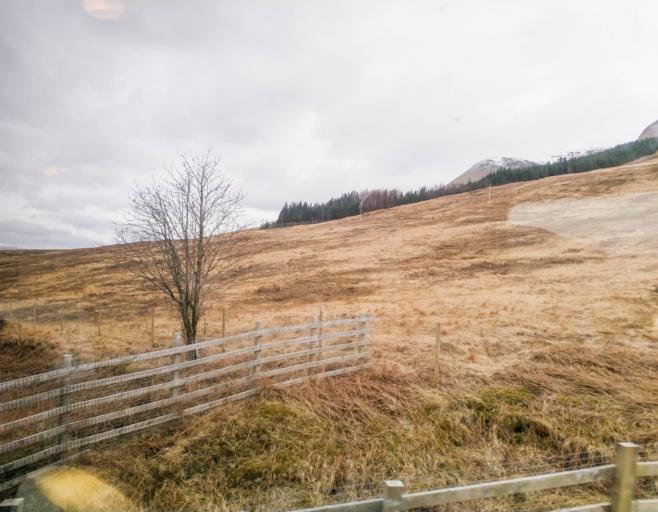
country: GB
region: Scotland
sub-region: Highland
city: Spean Bridge
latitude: 56.5039
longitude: -4.7555
